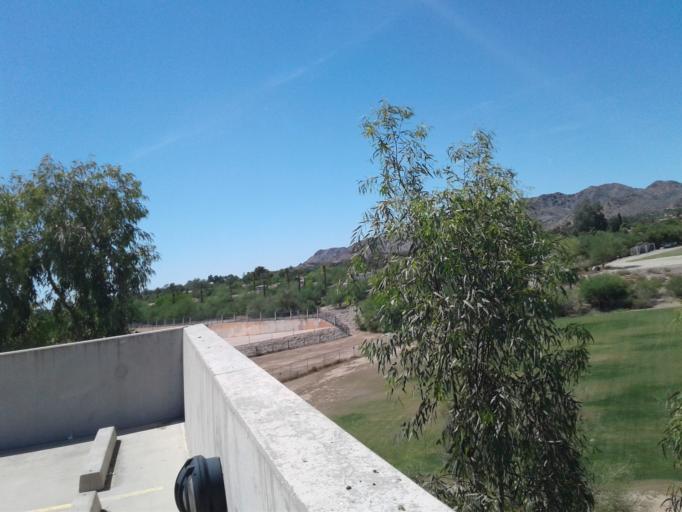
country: US
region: Arizona
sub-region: Maricopa County
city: Paradise Valley
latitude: 33.5135
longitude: -111.9989
